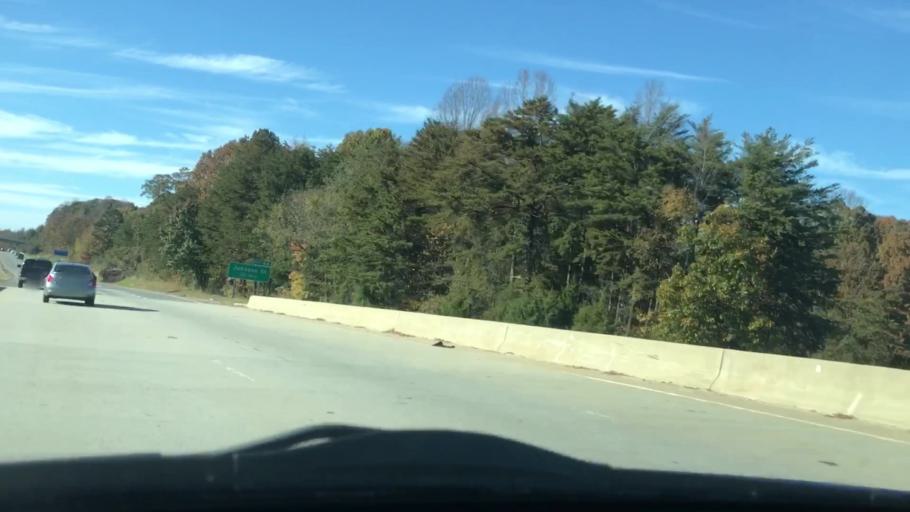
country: US
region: North Carolina
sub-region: Guilford County
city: High Point
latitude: 36.0057
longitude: -79.9971
